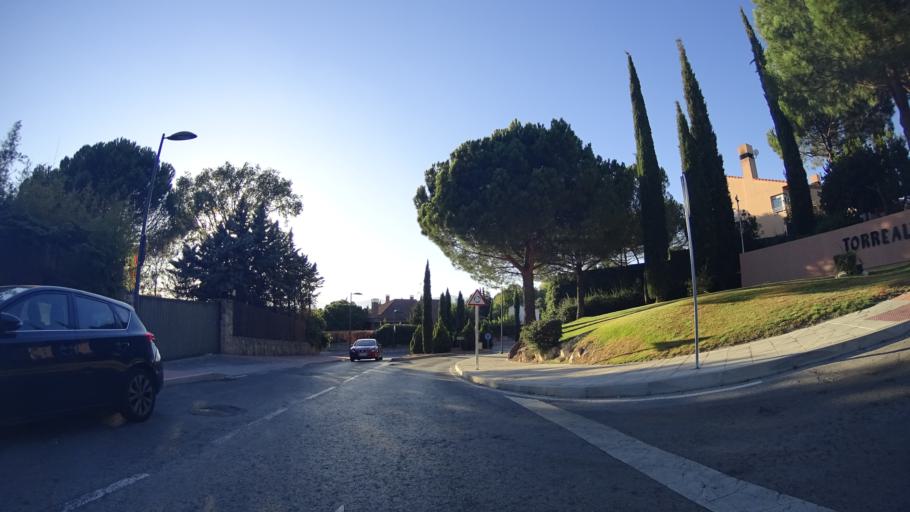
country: ES
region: Madrid
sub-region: Provincia de Madrid
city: Torrelodones
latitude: 40.5756
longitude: -3.9423
